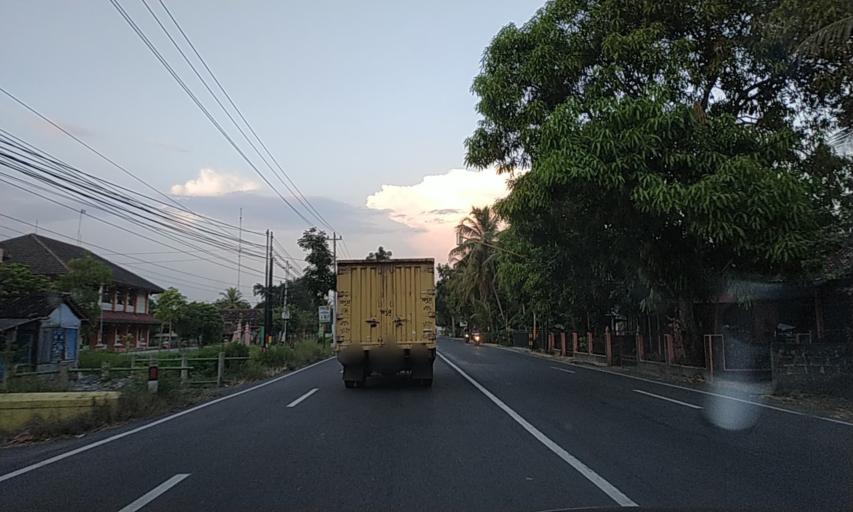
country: ID
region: Daerah Istimewa Yogyakarta
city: Srandakan
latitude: -7.8721
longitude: 110.1398
